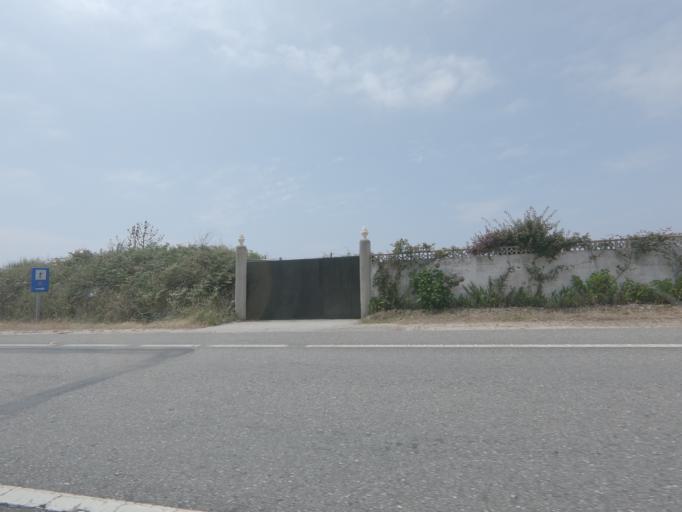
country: ES
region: Galicia
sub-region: Provincia de Pontevedra
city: A Guarda
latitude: 41.9410
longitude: -8.8840
